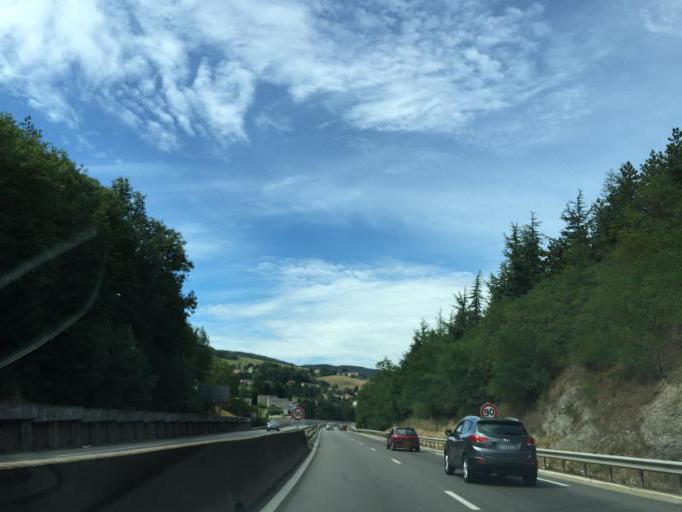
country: FR
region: Rhone-Alpes
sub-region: Departement de la Loire
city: Saint-Etienne
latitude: 45.4030
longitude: 4.3723
